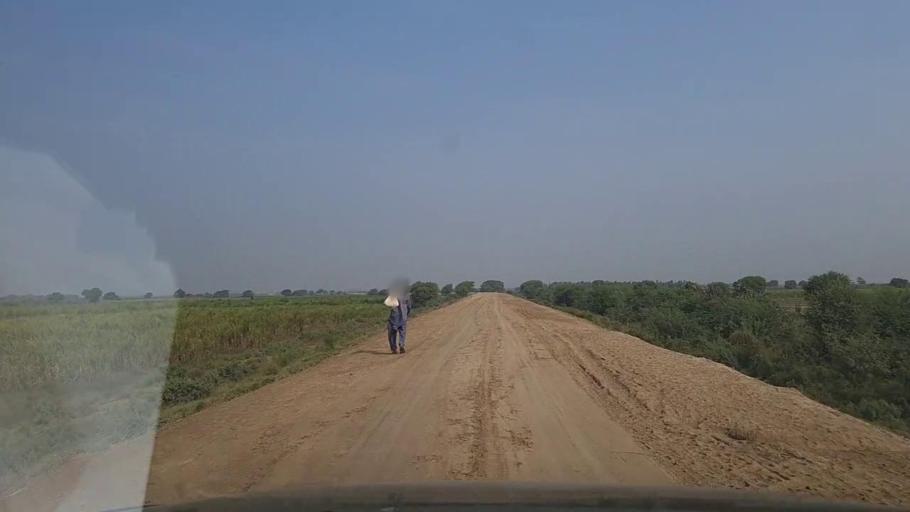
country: PK
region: Sindh
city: Bulri
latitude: 24.9840
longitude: 68.2938
